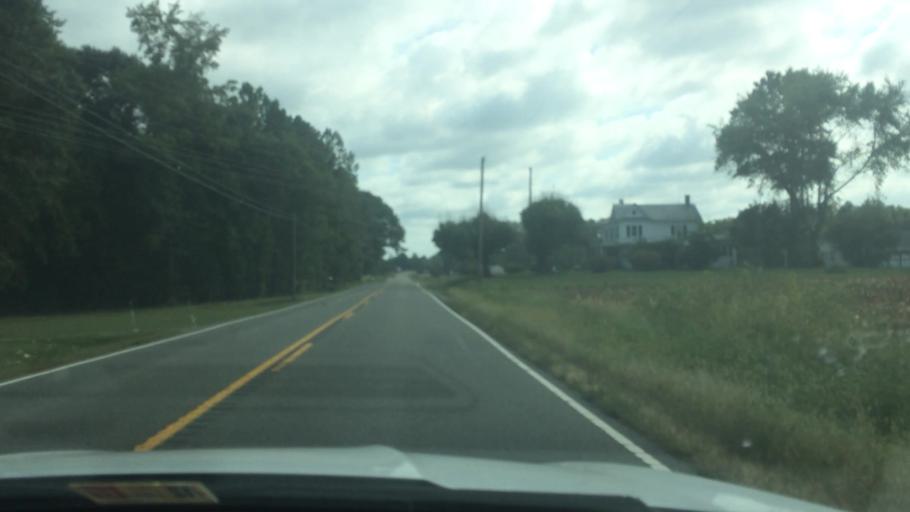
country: US
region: Virginia
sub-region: Northumberland County
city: Heathsville
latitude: 37.8445
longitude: -76.5802
